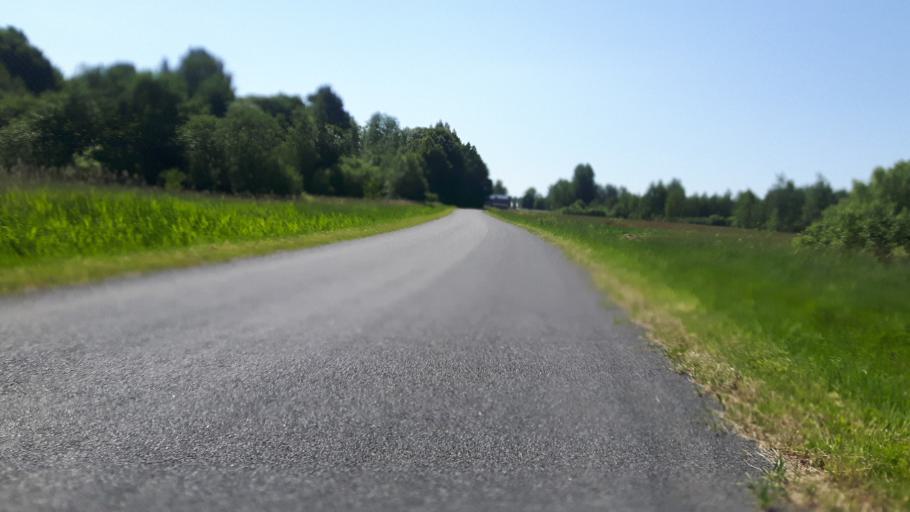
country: EE
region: Paernumaa
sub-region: Vaendra vald (alev)
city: Vandra
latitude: 58.5765
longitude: 24.9981
